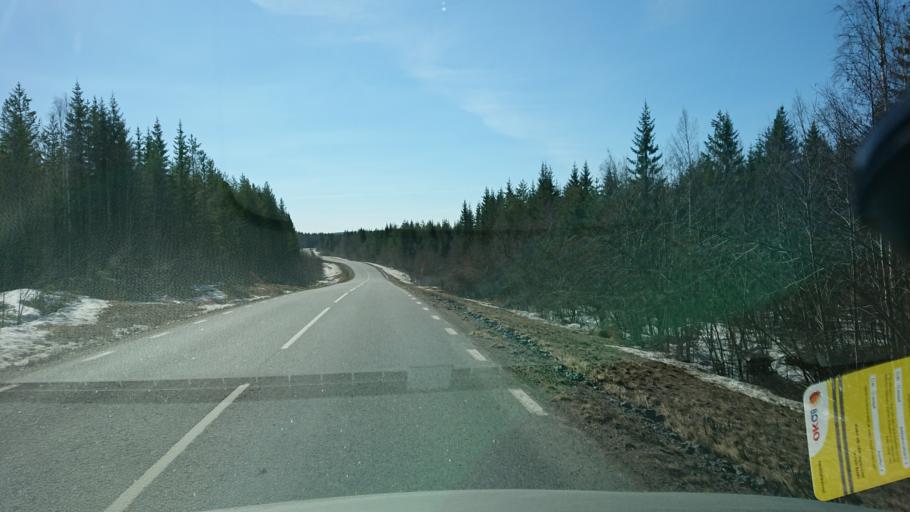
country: SE
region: Vaesternorrland
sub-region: Solleftea Kommun
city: As
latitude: 63.6838
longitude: 16.4324
